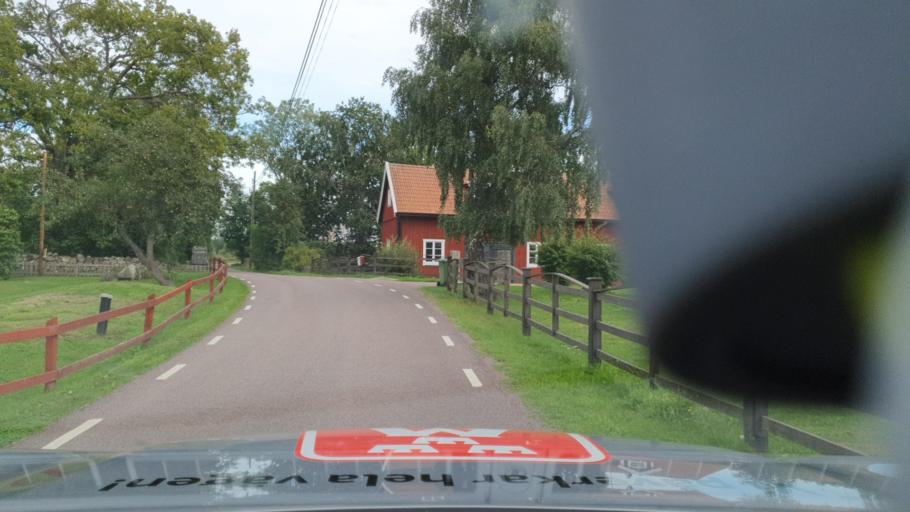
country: SE
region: Kalmar
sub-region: Kalmar Kommun
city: Lindsdal
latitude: 56.7720
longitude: 16.2397
